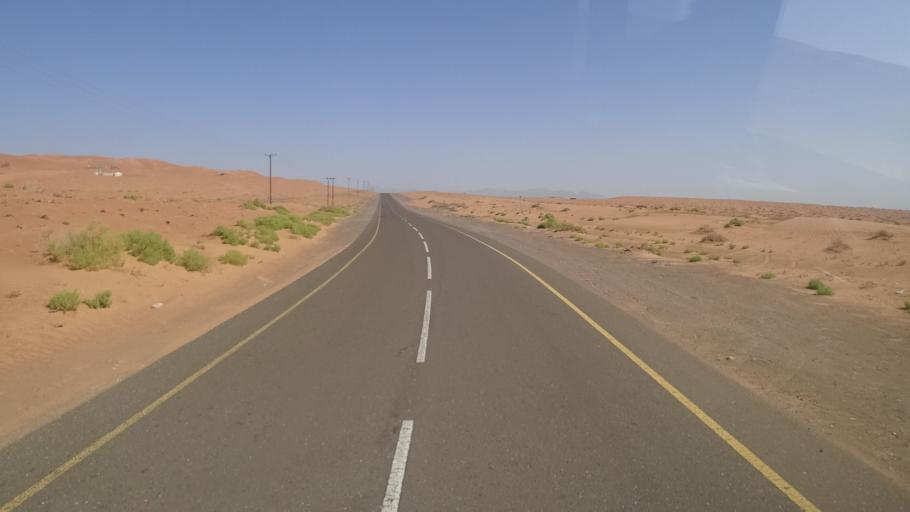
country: OM
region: Ash Sharqiyah
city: Al Qabil
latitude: 22.4883
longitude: 58.7149
